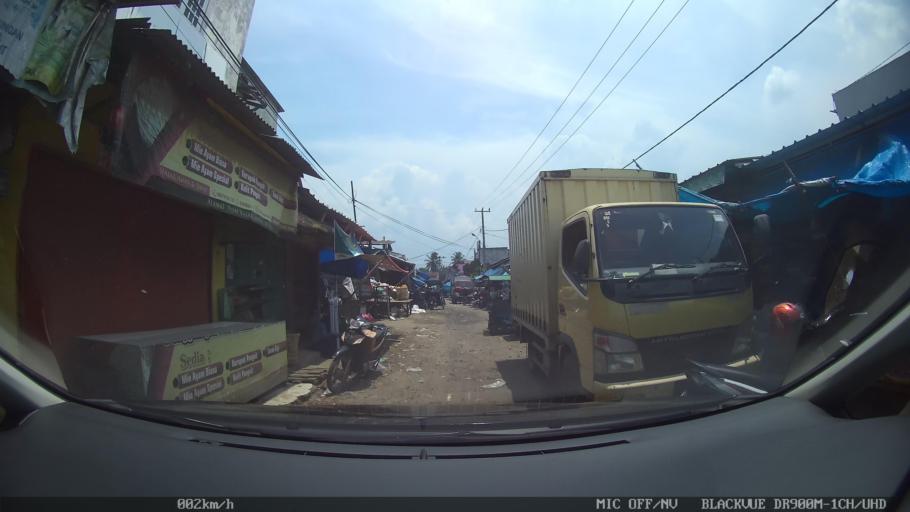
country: ID
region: Lampung
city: Natar
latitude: -5.3172
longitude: 105.1989
